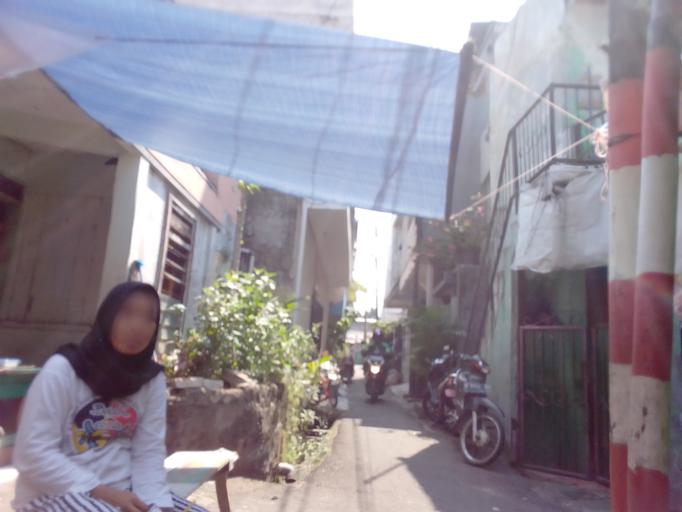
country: ID
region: Jakarta Raya
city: Jakarta
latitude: -6.2609
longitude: 106.8064
